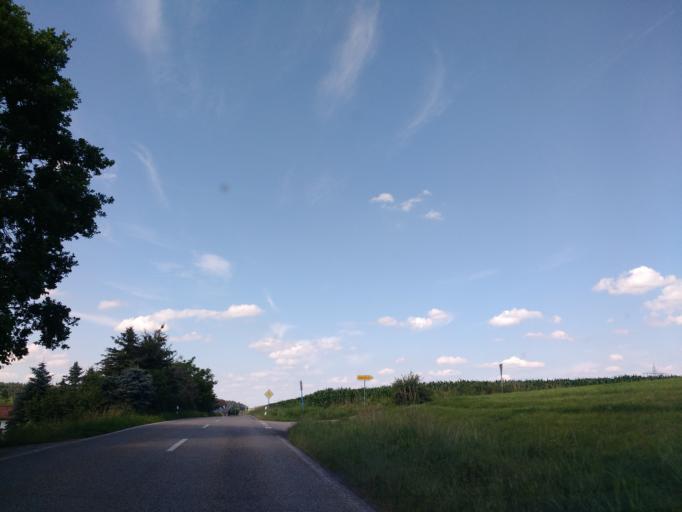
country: DE
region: Bavaria
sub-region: Upper Bavaria
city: Taufkirchen
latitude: 48.1183
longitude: 12.4185
